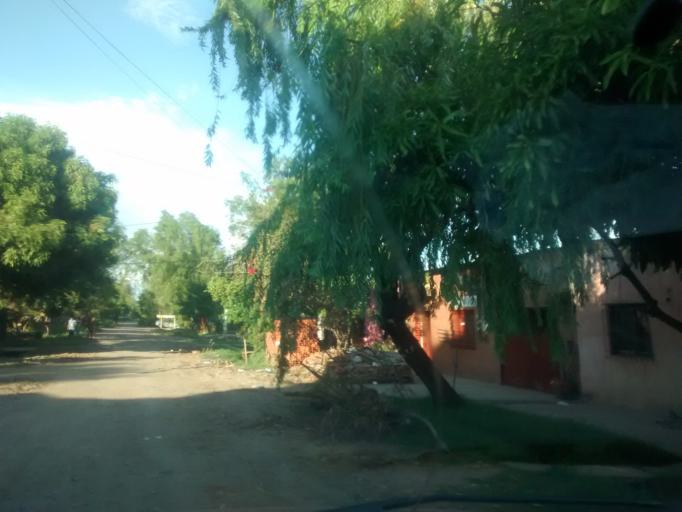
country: AR
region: Chaco
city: Resistencia
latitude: -27.4321
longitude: -58.9958
